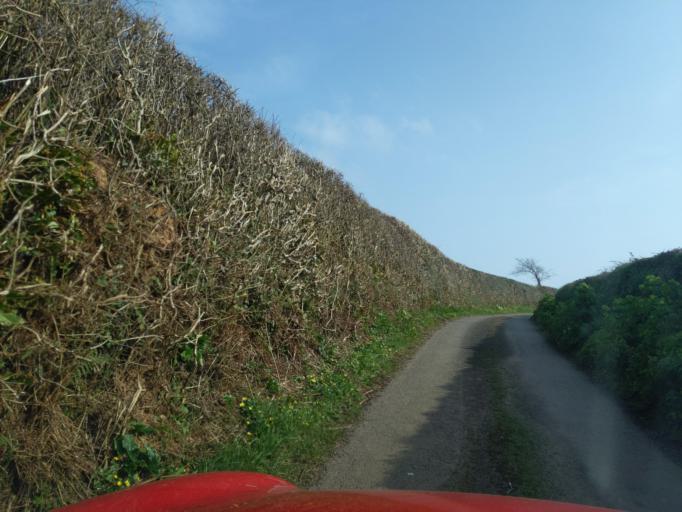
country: GB
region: England
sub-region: Devon
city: Kingsbridge
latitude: 50.2912
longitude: -3.7358
